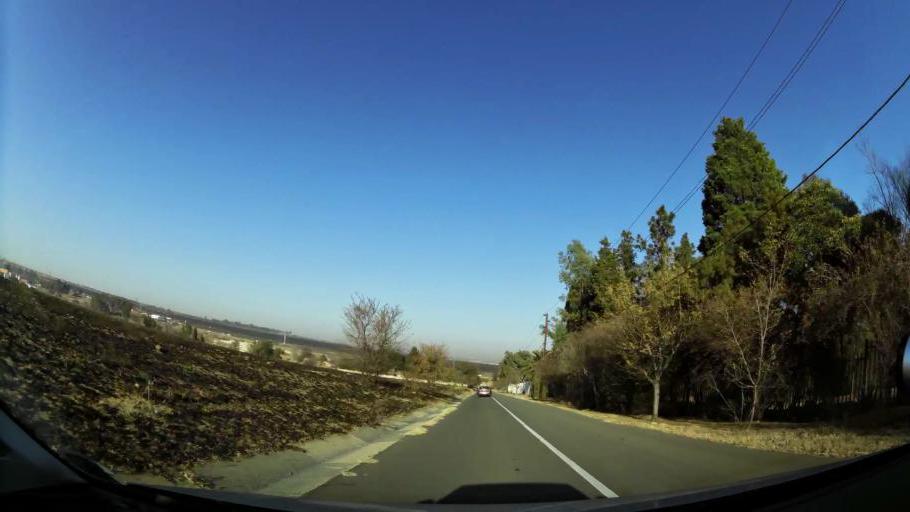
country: ZA
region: Gauteng
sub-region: City of Johannesburg Metropolitan Municipality
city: Midrand
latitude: -26.0262
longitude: 28.1374
